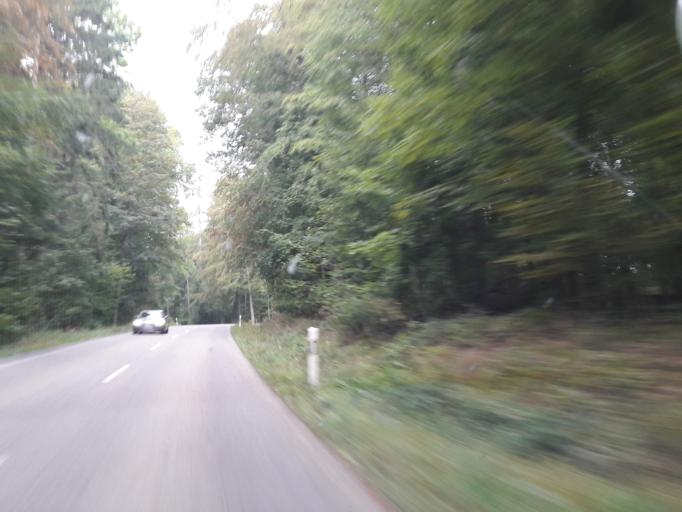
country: DE
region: Baden-Wuerttemberg
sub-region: Regierungsbezirk Stuttgart
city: Widdern
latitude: 49.2992
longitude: 9.3952
